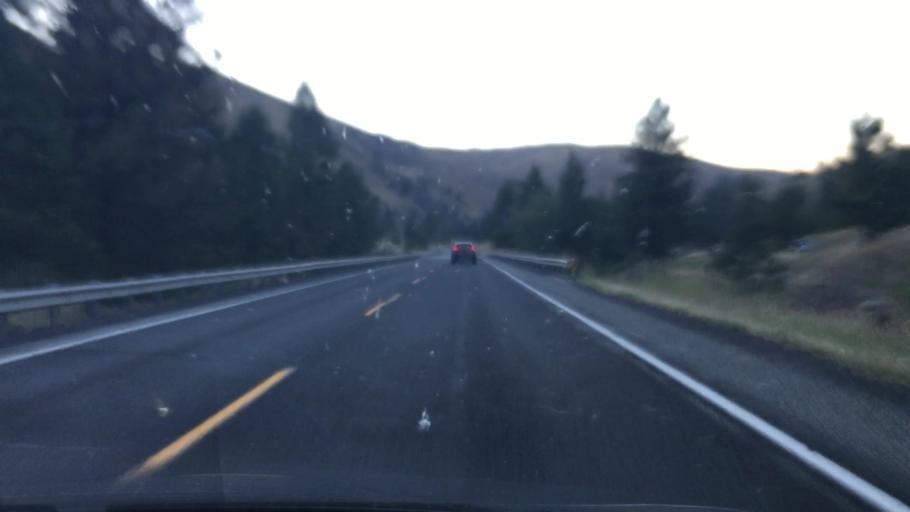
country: US
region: Idaho
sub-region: Valley County
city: McCall
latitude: 45.2954
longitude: -116.3585
